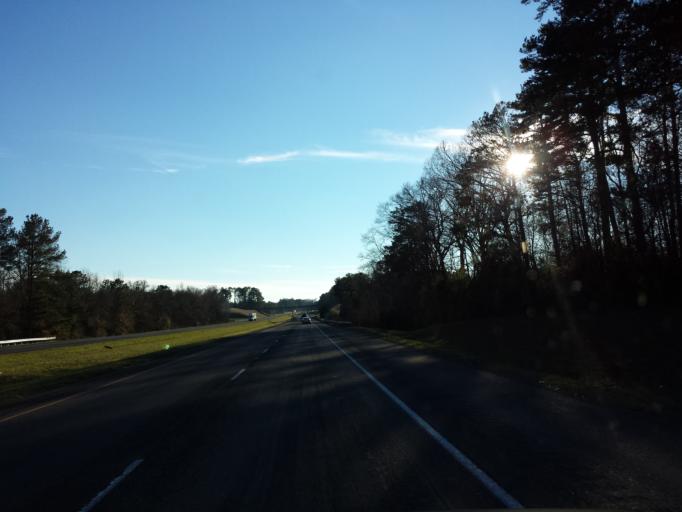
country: US
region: Alabama
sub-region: Greene County
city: Eutaw
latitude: 32.9217
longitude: -87.8664
